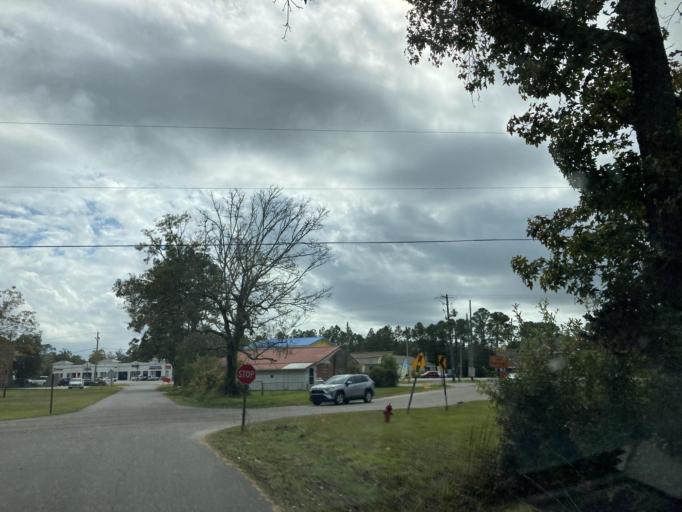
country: US
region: Mississippi
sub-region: Jackson County
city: Gulf Hills
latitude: 30.4392
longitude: -88.8328
